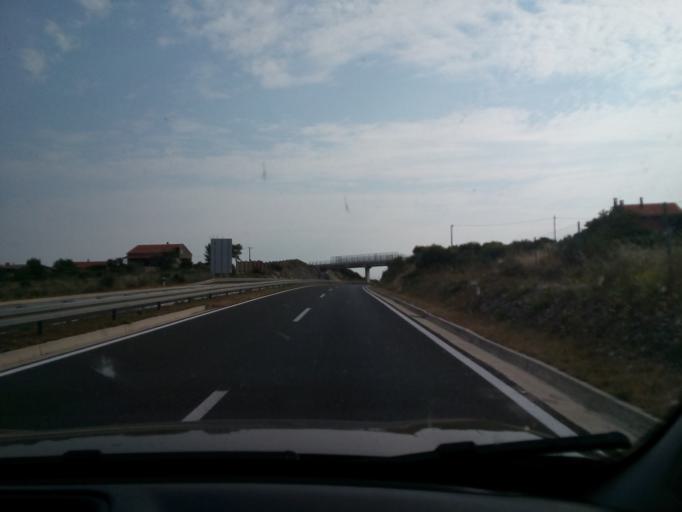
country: HR
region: Zadarska
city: Bibinje
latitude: 44.0961
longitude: 15.2848
